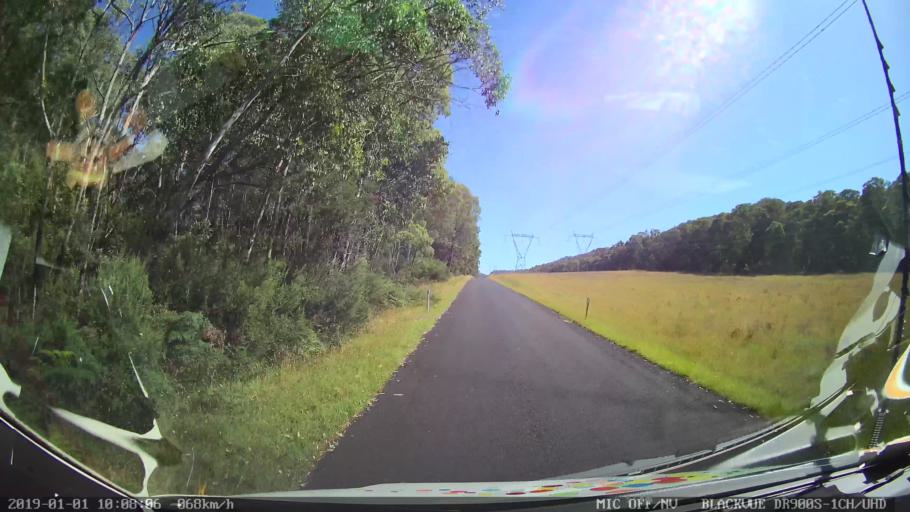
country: AU
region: New South Wales
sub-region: Snowy River
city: Jindabyne
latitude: -36.1627
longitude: 148.1573
